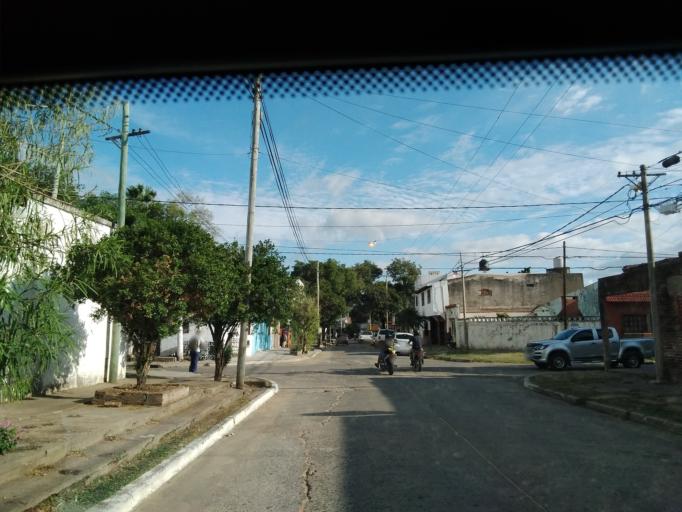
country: AR
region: Corrientes
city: Corrientes
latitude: -27.4653
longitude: -58.8194
